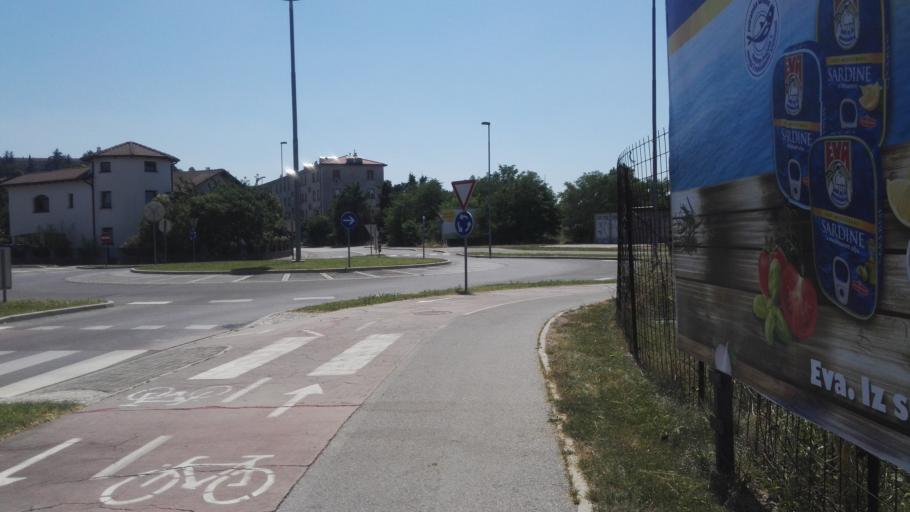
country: SI
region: Nova Gorica
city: Nova Gorica
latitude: 45.9560
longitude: 13.6382
